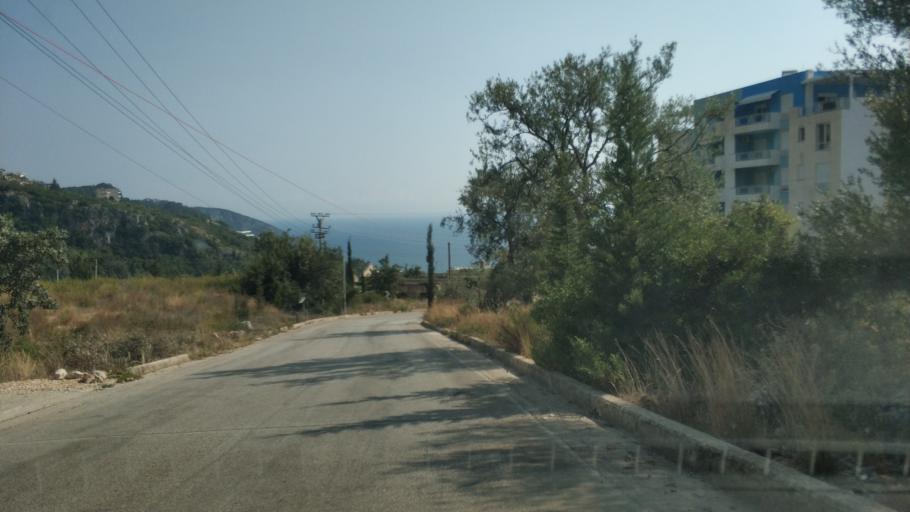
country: AL
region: Vlore
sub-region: Rrethi i Vlores
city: Vranisht
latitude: 40.1508
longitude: 19.6345
